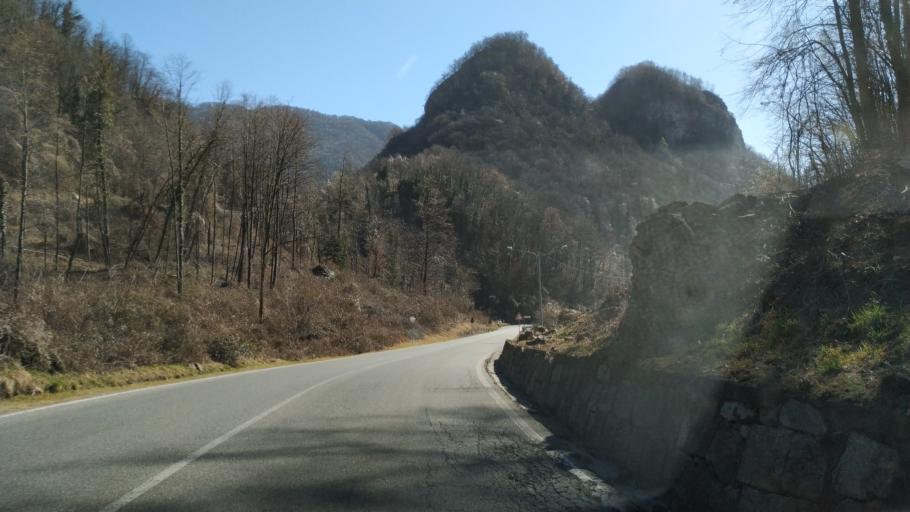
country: IT
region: Piedmont
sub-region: Provincia di Vercelli
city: Varallo
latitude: 45.8049
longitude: 8.2726
